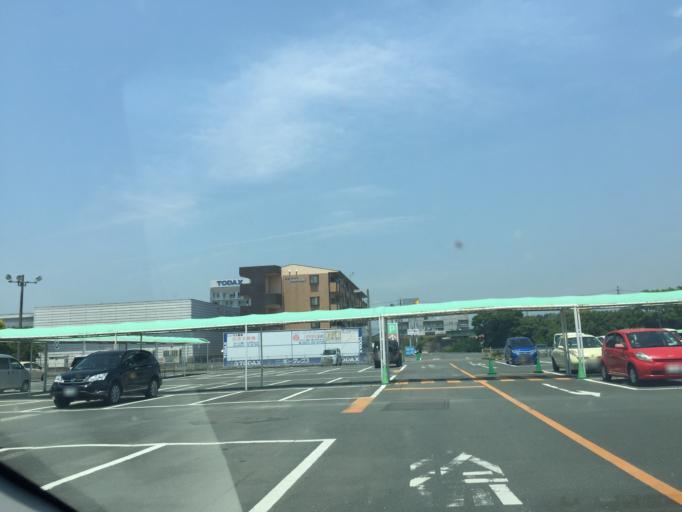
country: JP
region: Shizuoka
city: Kakegawa
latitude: 34.7725
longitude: 137.9888
